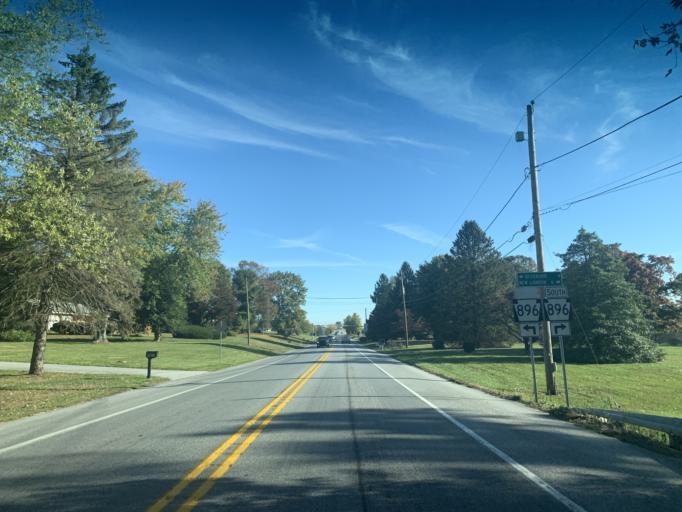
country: US
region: Pennsylvania
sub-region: Chester County
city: Oxford
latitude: 39.8404
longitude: -75.9416
